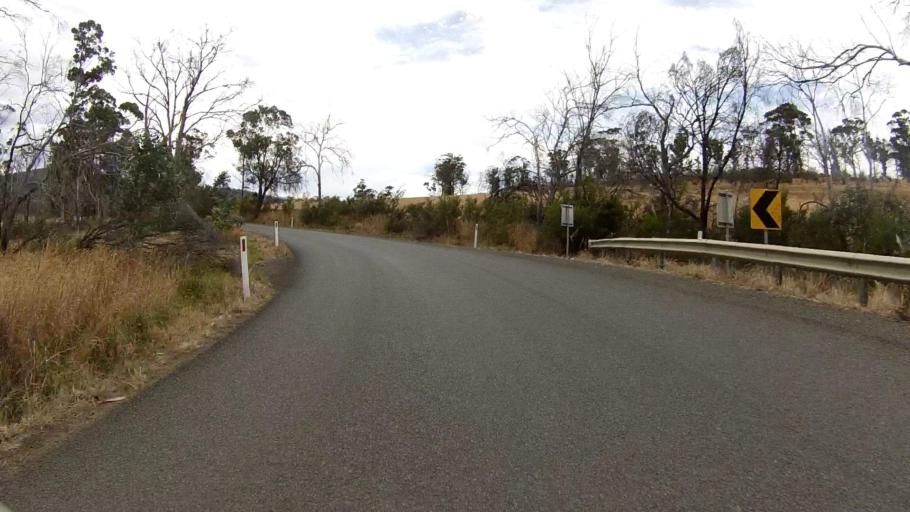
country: AU
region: Tasmania
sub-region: Sorell
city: Sorell
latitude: -42.8949
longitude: 147.7788
